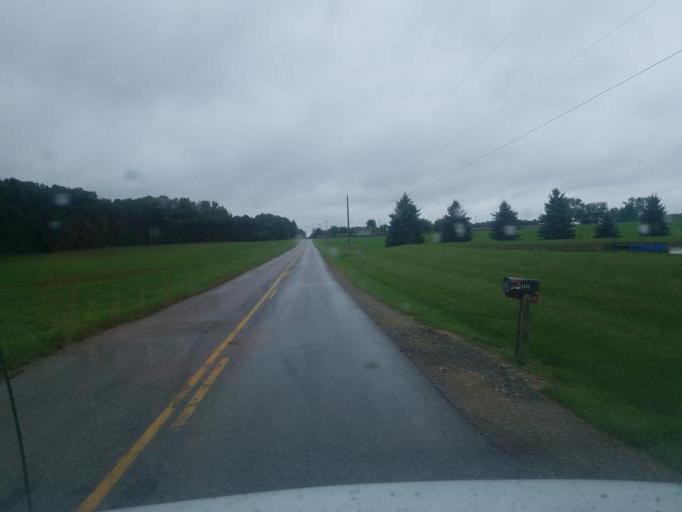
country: US
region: Ohio
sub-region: Wayne County
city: West Salem
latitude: 40.8451
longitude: -82.1747
